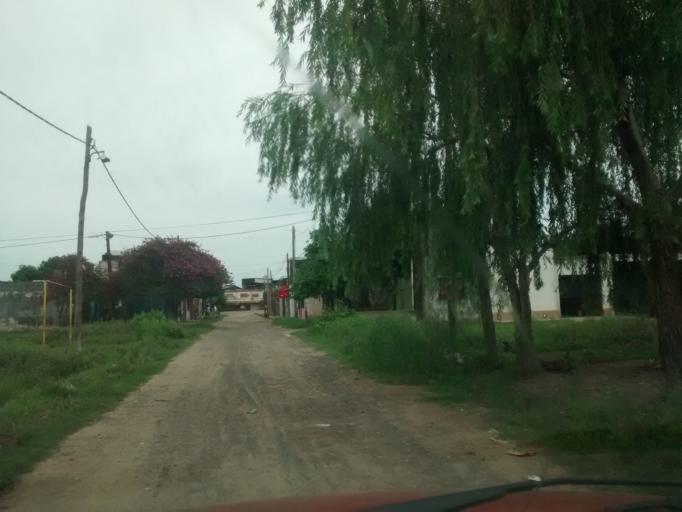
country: AR
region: Chaco
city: Resistencia
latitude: -27.4243
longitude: -58.9753
